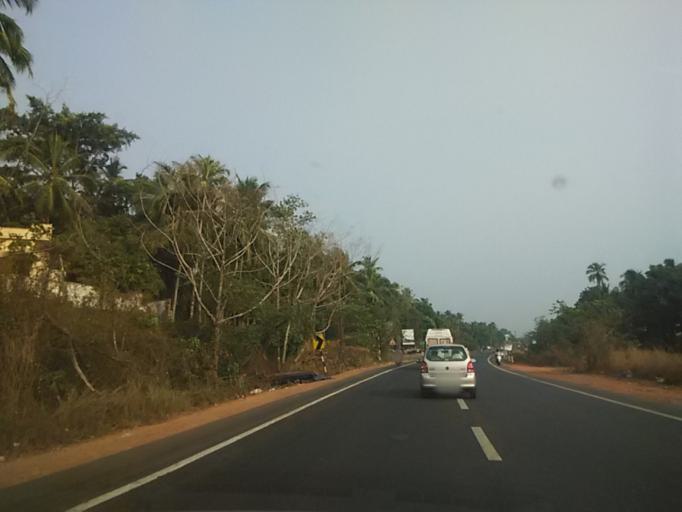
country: IN
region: Kerala
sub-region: Kozhikode
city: Kozhikode
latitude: 11.3072
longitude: 75.7867
